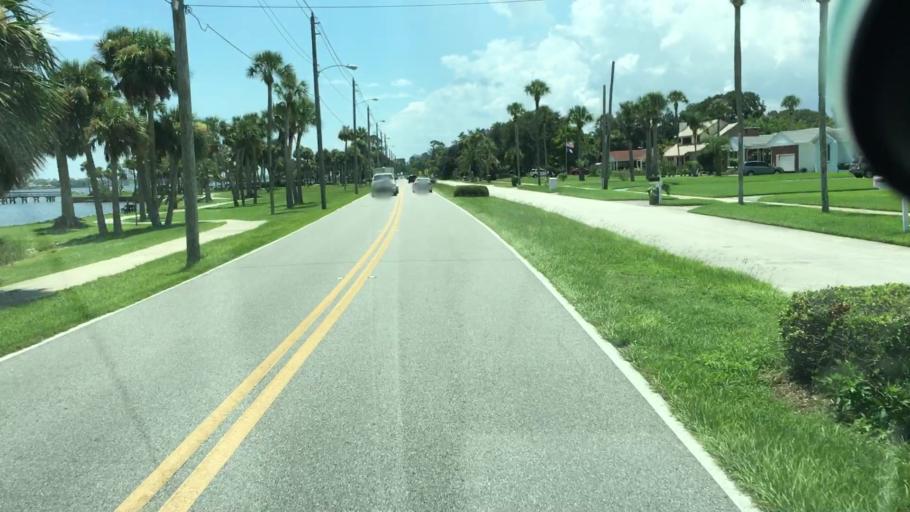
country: US
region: Florida
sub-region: Volusia County
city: Ormond Beach
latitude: 29.2656
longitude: -81.0457
